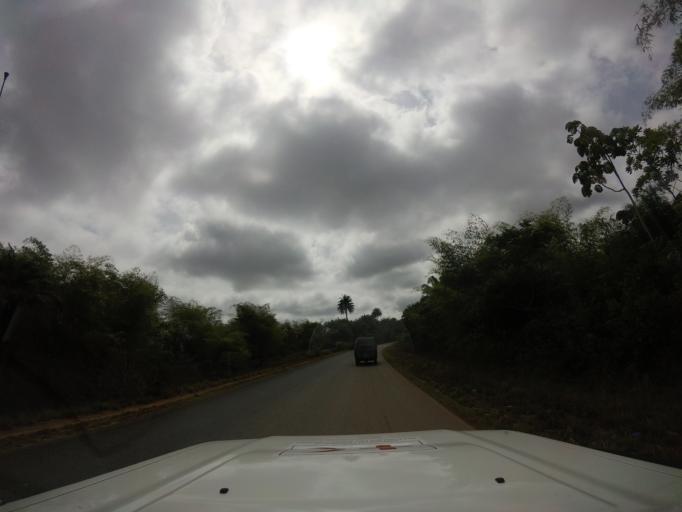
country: LR
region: Montserrado
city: Monrovia
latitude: 6.5231
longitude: -10.8321
